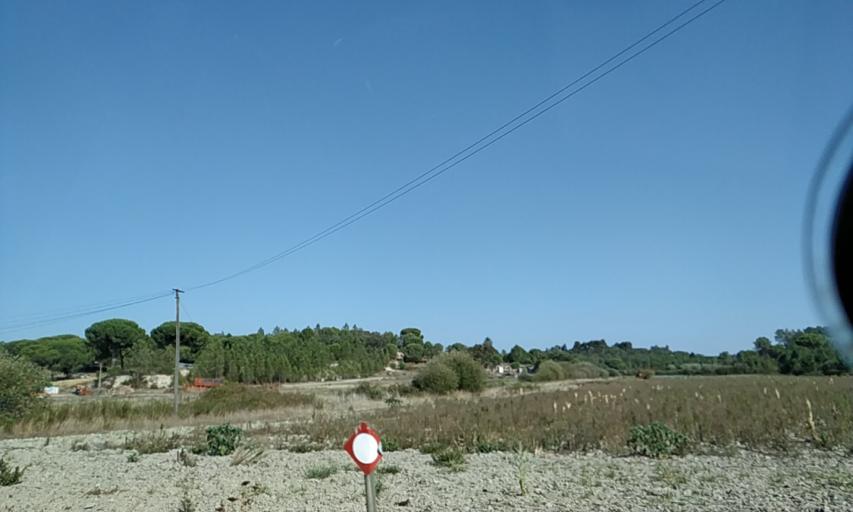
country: PT
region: Santarem
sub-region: Coruche
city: Coruche
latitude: 38.8851
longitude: -8.5369
